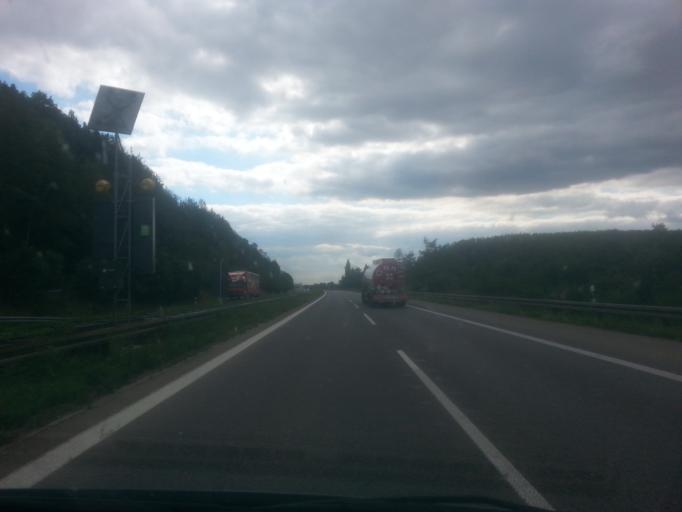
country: DE
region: Bavaria
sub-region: Upper Palatinate
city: Nabburg
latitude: 49.4261
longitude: 12.1719
